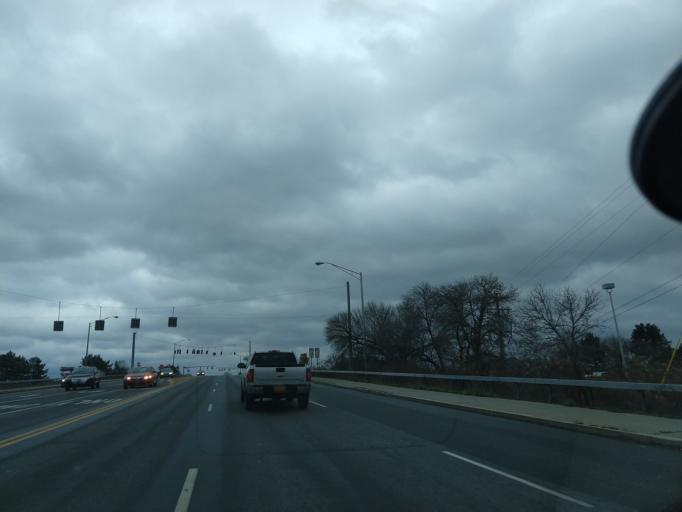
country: US
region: New York
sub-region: Tompkins County
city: Lansing
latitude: 42.4826
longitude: -76.4850
